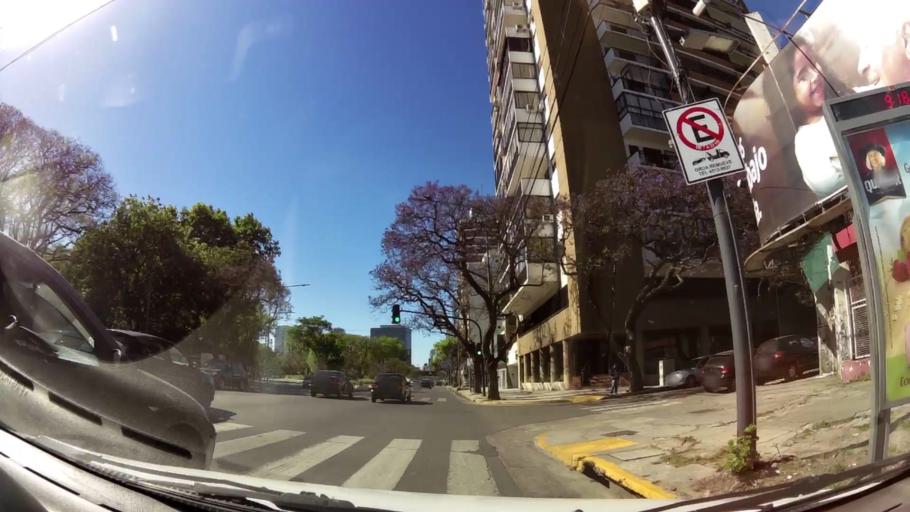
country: AR
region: Buenos Aires
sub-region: Partido de Vicente Lopez
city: Olivos
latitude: -34.5285
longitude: -58.4707
